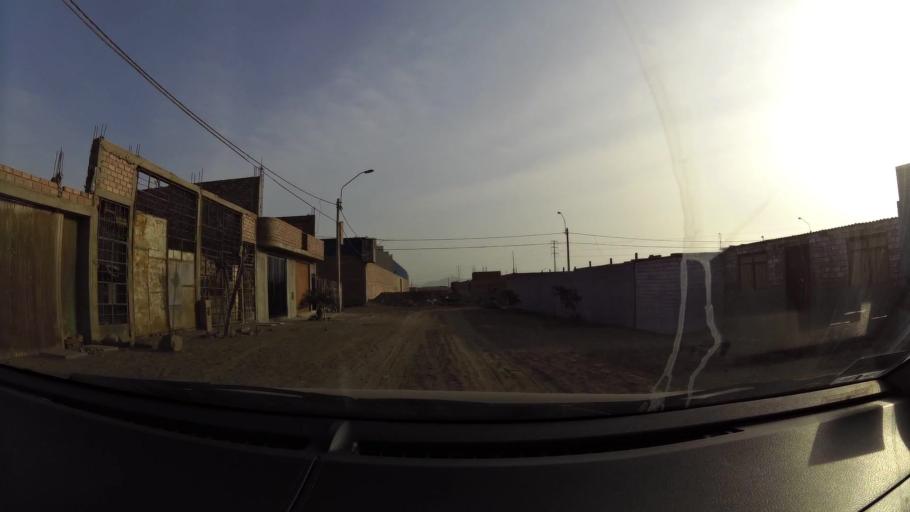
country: PE
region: Lima
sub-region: Lima
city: Santa Rosa
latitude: -11.7490
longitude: -77.1489
